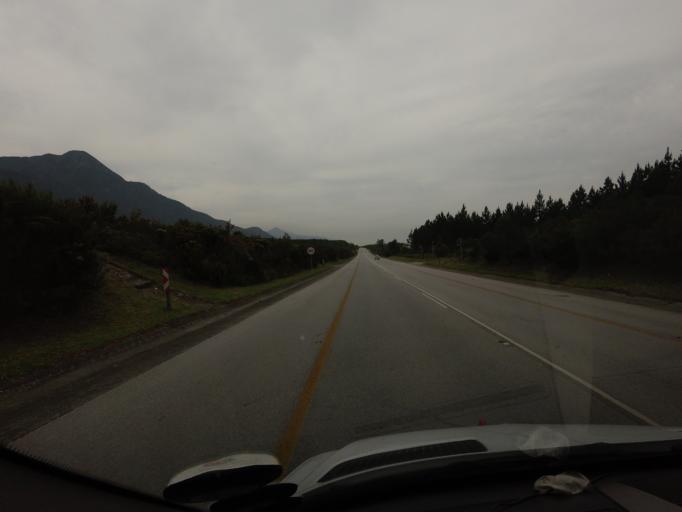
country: ZA
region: Eastern Cape
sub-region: Cacadu District Municipality
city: Kareedouw
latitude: -33.9650
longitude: 23.8704
